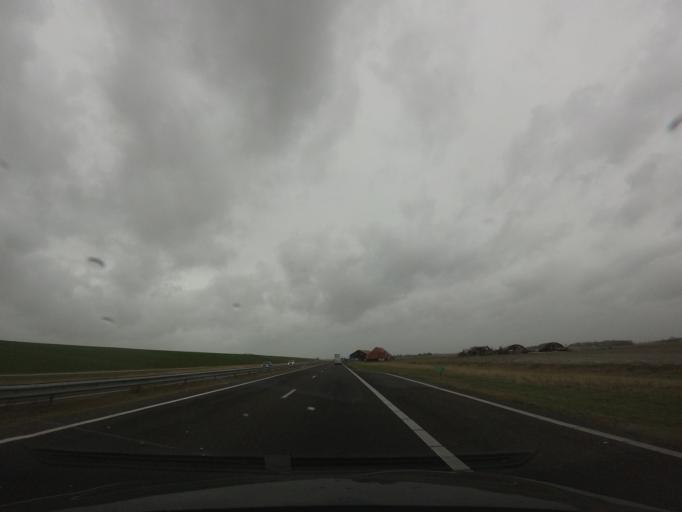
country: NL
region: Friesland
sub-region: Gemeente Harlingen
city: Harlingen
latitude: 53.1344
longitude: 5.4111
